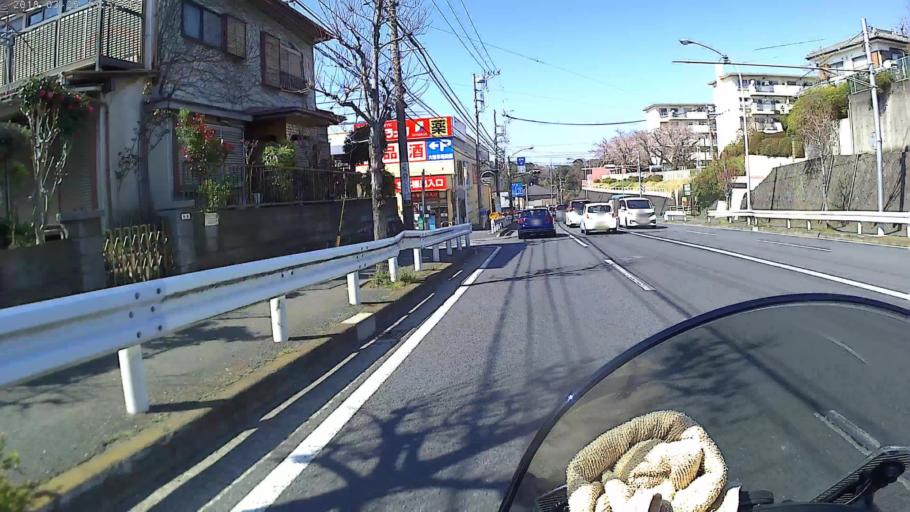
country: JP
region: Kanagawa
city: Fujisawa
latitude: 35.3808
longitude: 139.5027
